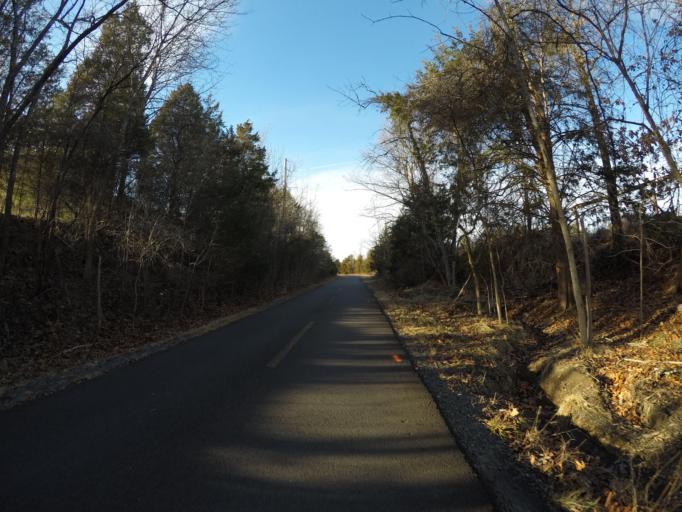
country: US
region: Virginia
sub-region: Loudoun County
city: Leesburg
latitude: 39.1007
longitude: -77.5475
